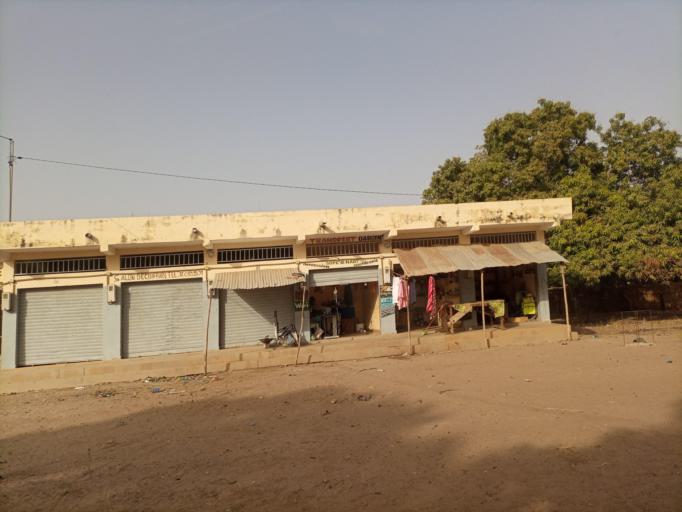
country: SN
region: Fatick
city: Passi
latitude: 14.0196
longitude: -16.2953
